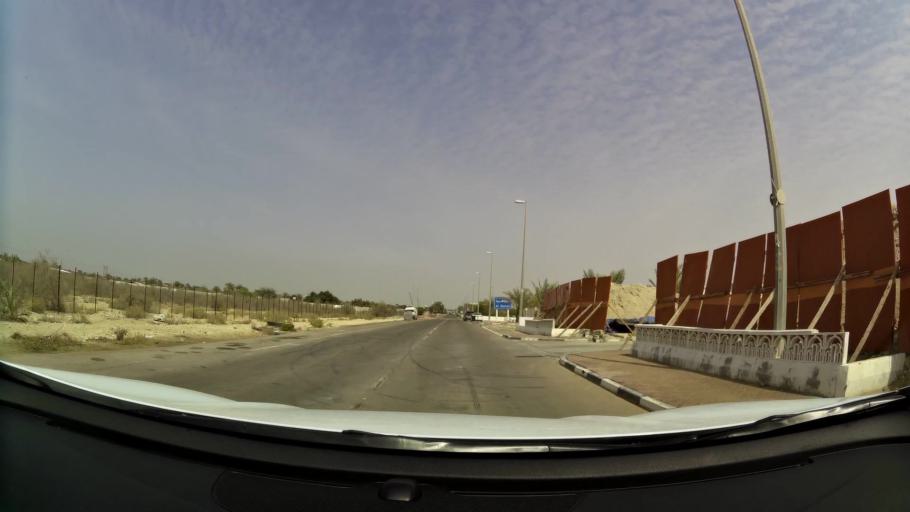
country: AE
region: Abu Dhabi
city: Abu Dhabi
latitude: 24.5284
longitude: 54.6647
